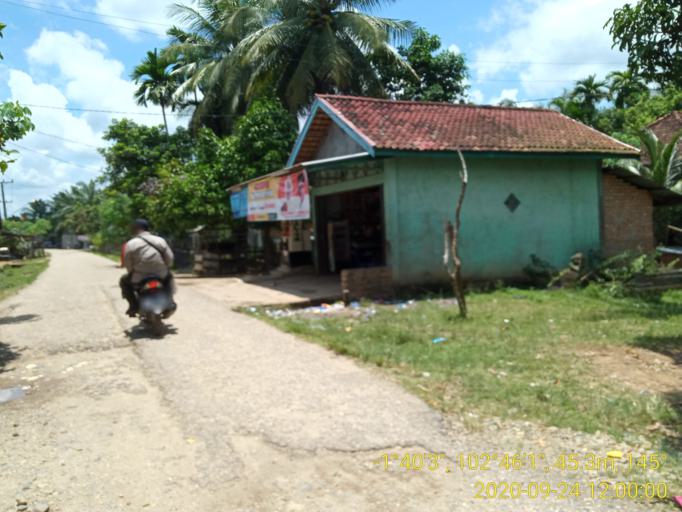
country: ID
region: Jambi
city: Sungaibengkal
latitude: -1.6676
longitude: 102.7672
